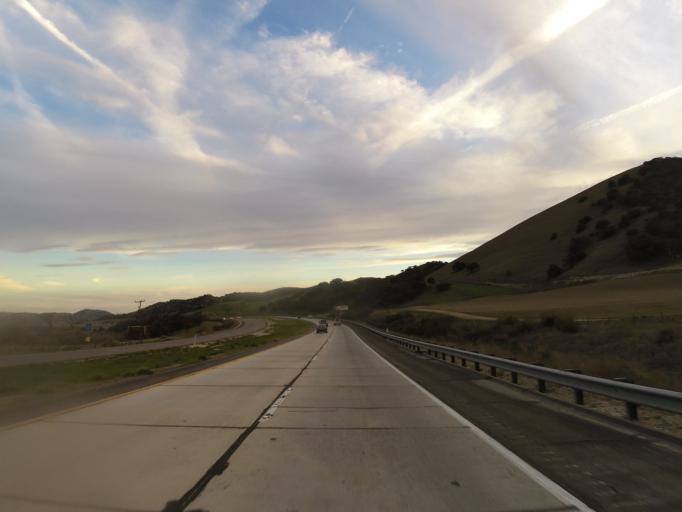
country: US
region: California
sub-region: San Luis Obispo County
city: Lake Nacimiento
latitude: 35.9290
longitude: -120.8702
